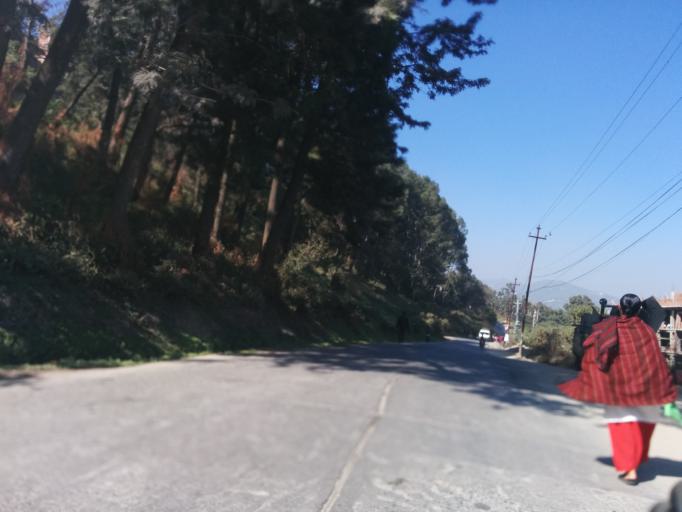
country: NP
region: Central Region
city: Kirtipur
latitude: 27.6804
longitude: 85.2764
